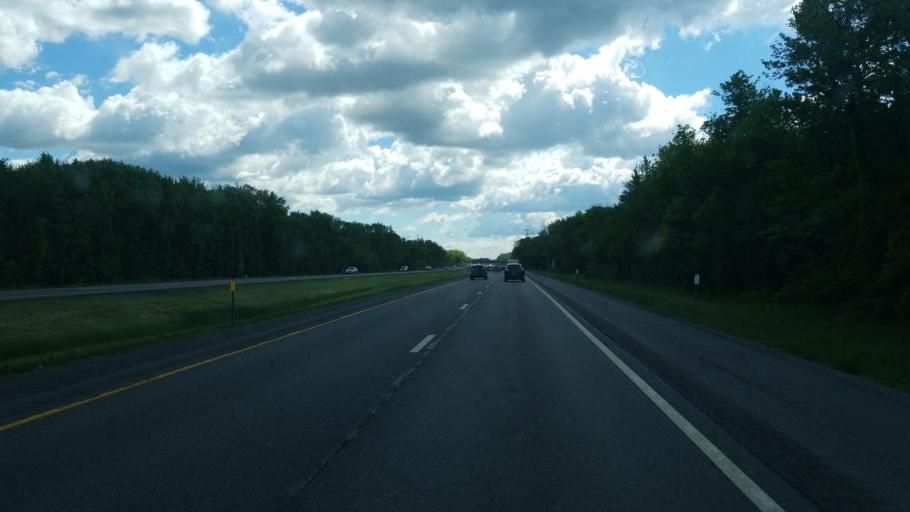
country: US
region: New York
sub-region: Onondaga County
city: Minoa
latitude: 43.0944
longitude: -76.0136
